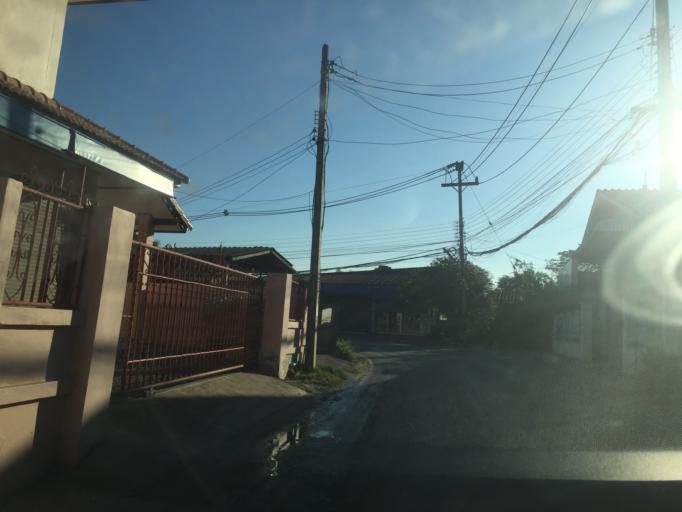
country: TH
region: Lamphun
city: Lamphun
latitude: 18.6065
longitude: 99.0578
